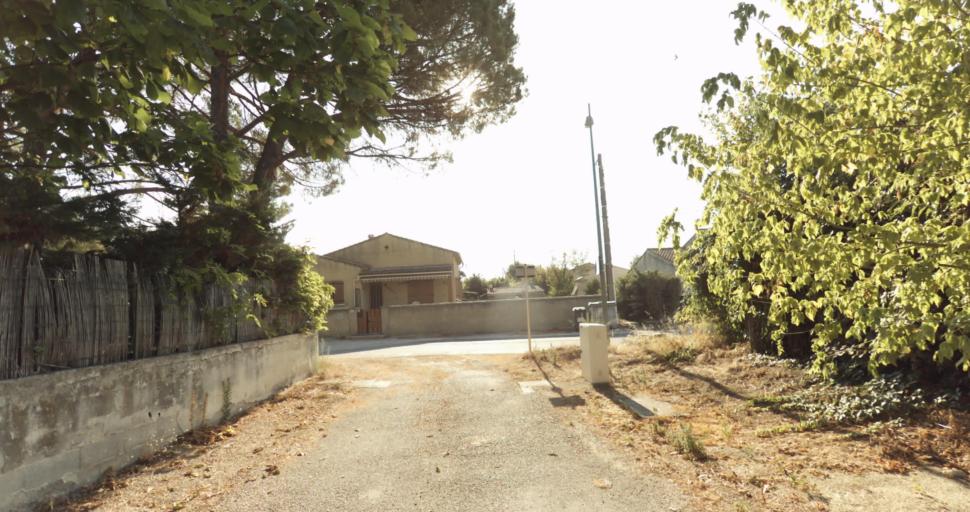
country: FR
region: Provence-Alpes-Cote d'Azur
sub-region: Departement du Vaucluse
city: Monteux
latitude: 44.0294
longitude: 4.9963
